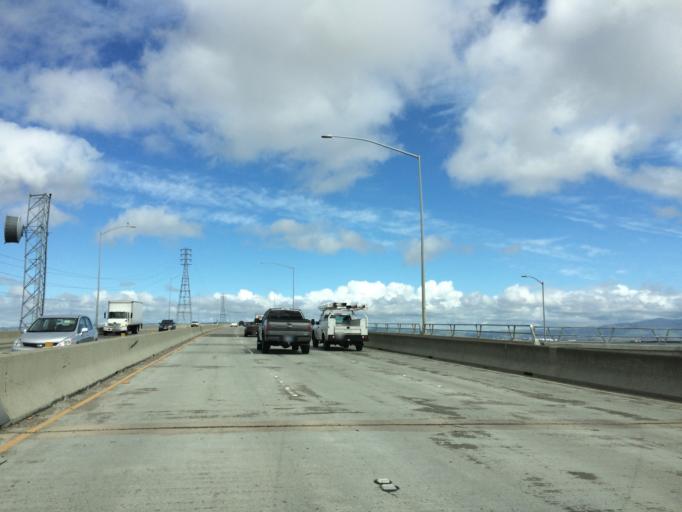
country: US
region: California
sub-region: San Mateo County
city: East Palo Alto
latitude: 37.4987
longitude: -122.1291
